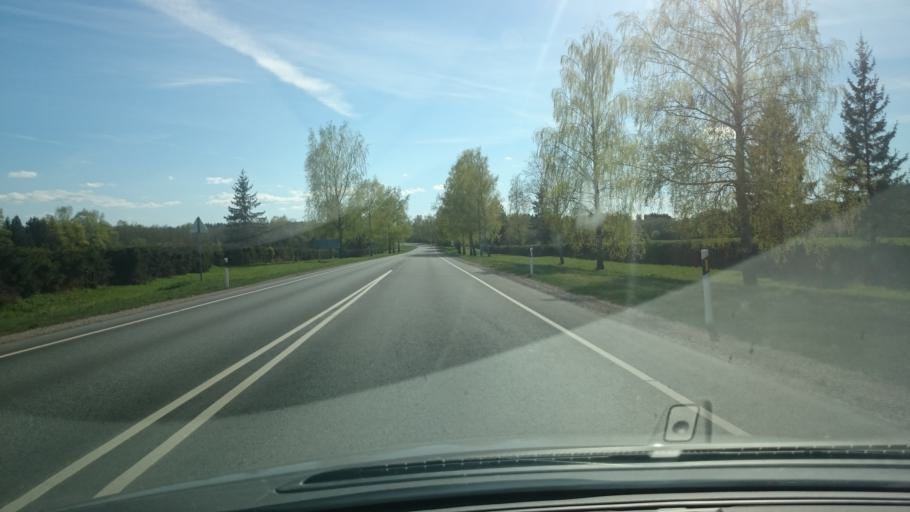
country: EE
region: Laeaene-Virumaa
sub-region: Kadrina vald
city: Kadrina
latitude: 59.3304
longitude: 26.1065
